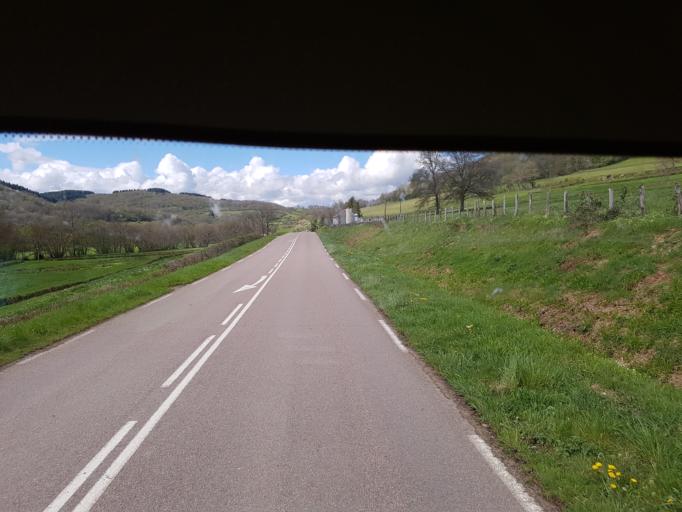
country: FR
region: Bourgogne
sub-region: Departement de Saone-et-Loire
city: Autun
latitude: 47.0926
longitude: 4.2371
